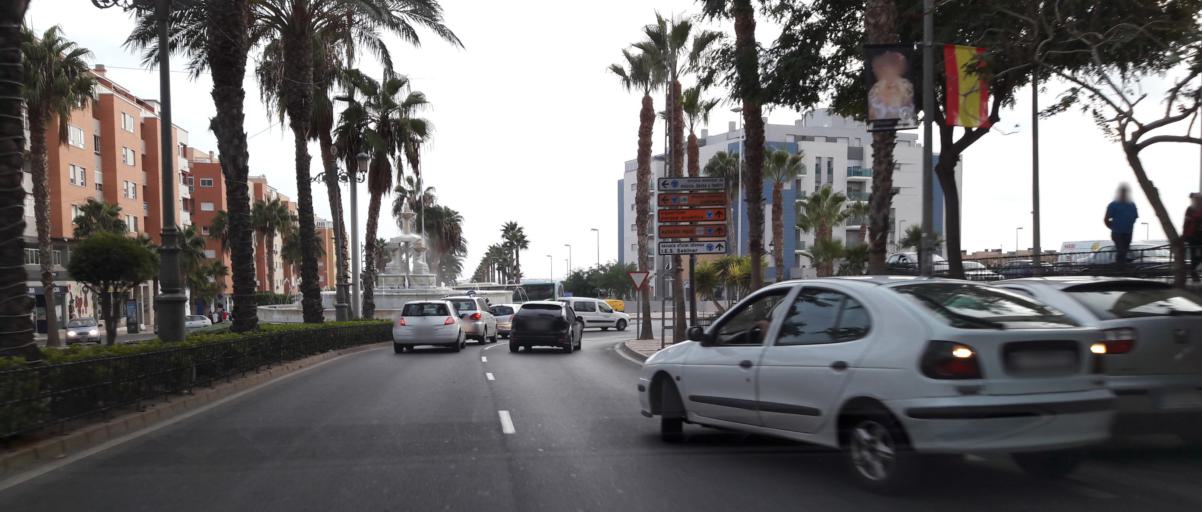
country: ES
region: Andalusia
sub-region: Provincia de Almeria
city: Aguadulce
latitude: 36.8039
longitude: -2.5996
